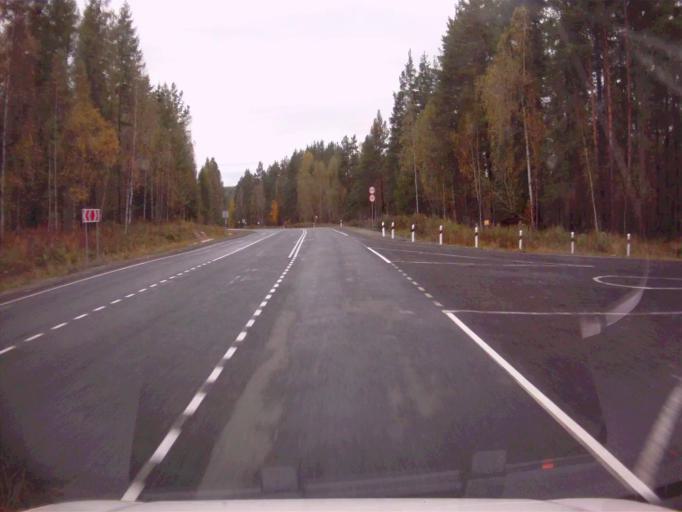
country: RU
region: Chelyabinsk
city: Nyazepetrovsk
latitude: 56.0611
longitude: 59.7295
